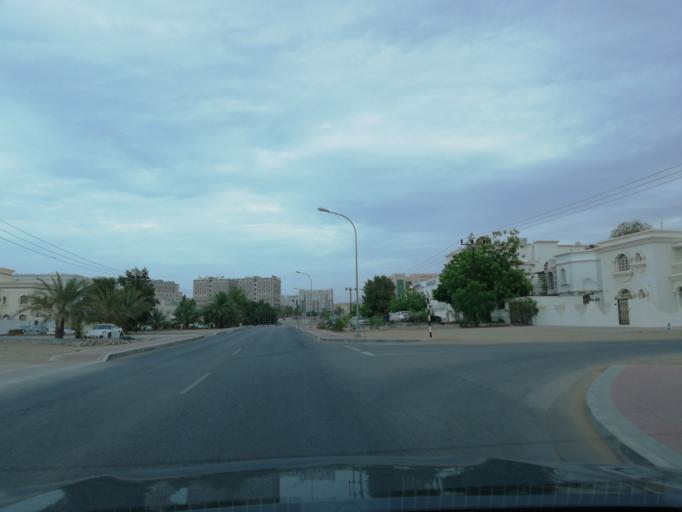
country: OM
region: Muhafazat Masqat
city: Bawshar
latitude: 23.5807
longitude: 58.4041
